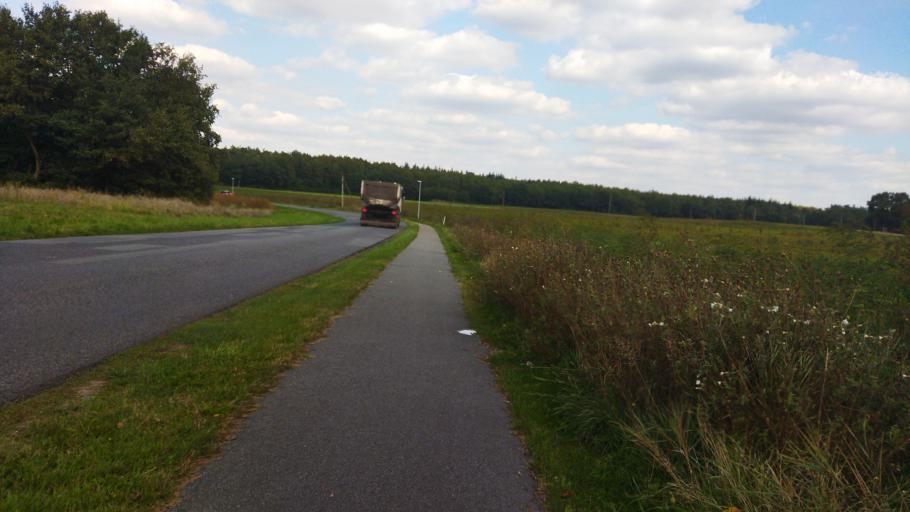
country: DE
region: Lower Saxony
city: Haren
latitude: 52.8049
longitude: 7.2687
